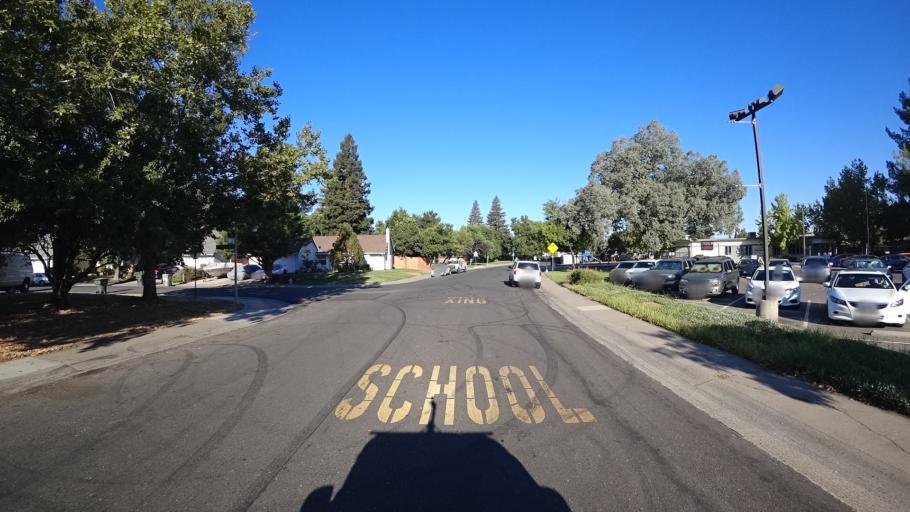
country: US
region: California
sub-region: Sacramento County
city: Florin
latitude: 38.4624
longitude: -121.4229
